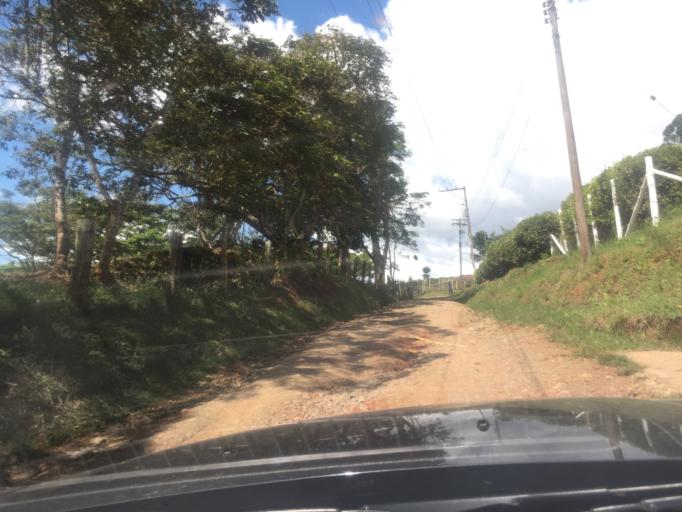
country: CO
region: Valle del Cauca
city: Yumbo
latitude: 3.6609
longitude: -76.5544
